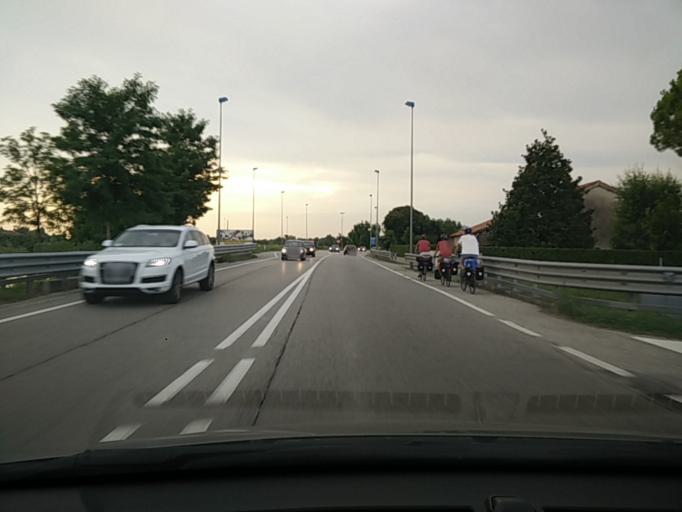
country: IT
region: Veneto
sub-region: Provincia di Venezia
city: Passarella
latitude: 45.5544
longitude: 12.5863
